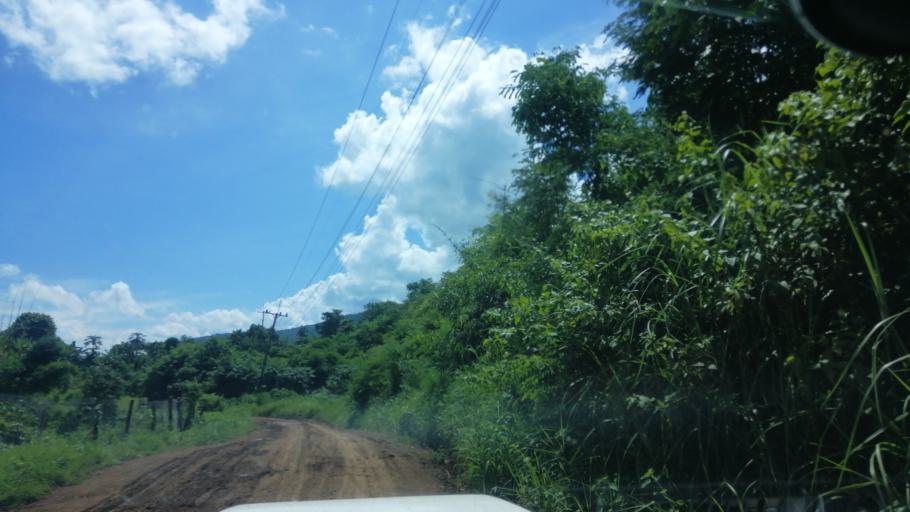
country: TH
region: Uttaradit
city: Ban Khok
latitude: 18.0984
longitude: 101.2516
